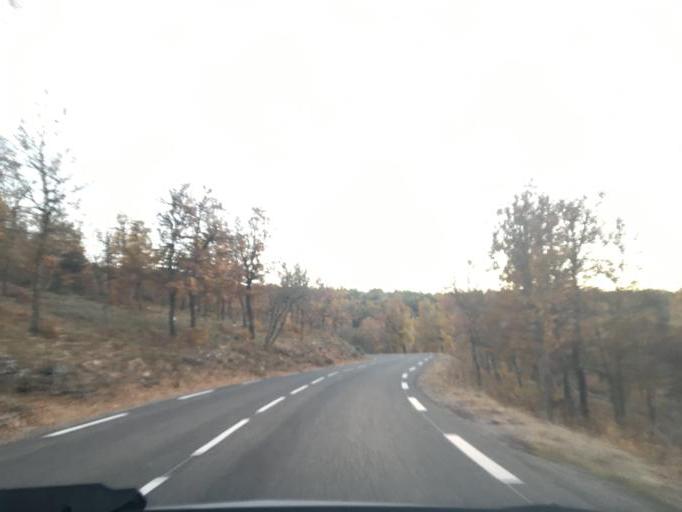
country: FR
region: Provence-Alpes-Cote d'Azur
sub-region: Departement du Var
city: Montferrat
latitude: 43.6652
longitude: 6.4859
